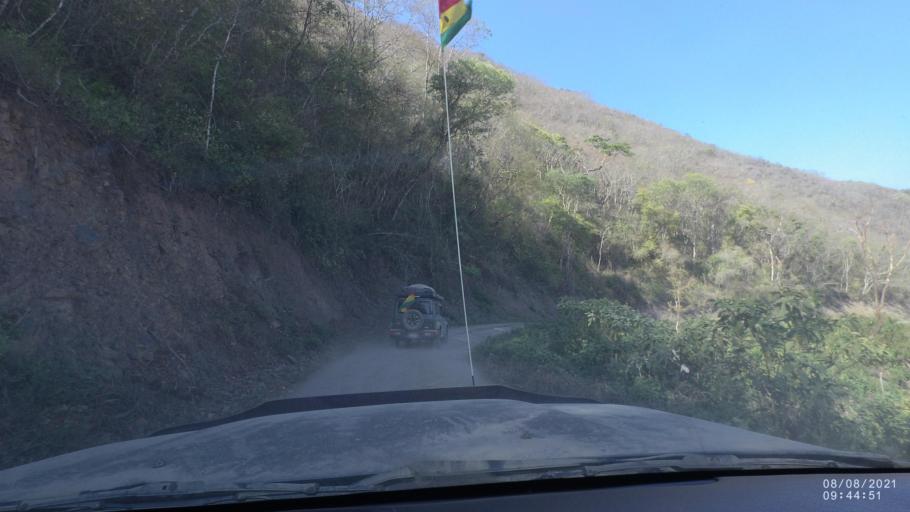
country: BO
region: La Paz
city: Quime
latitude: -16.6023
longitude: -66.7247
